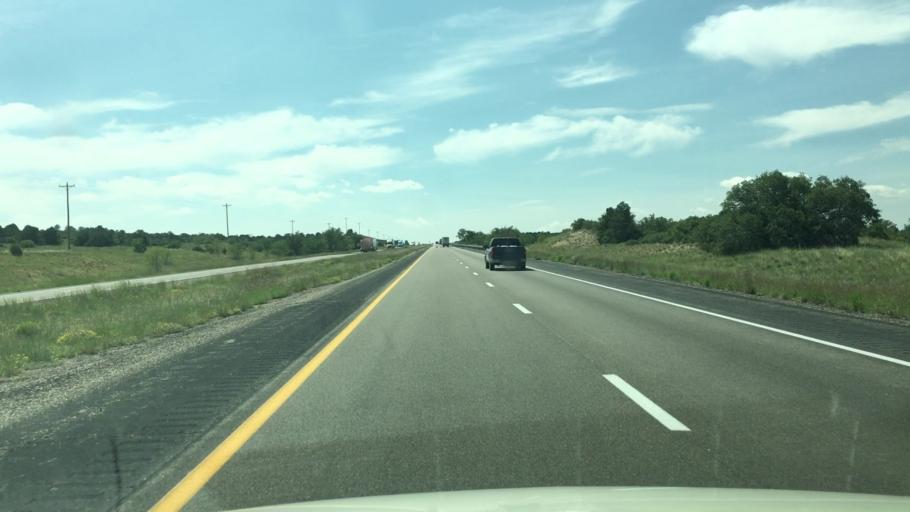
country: US
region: New Mexico
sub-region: San Miguel County
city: Las Vegas
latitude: 34.9924
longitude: -105.3094
